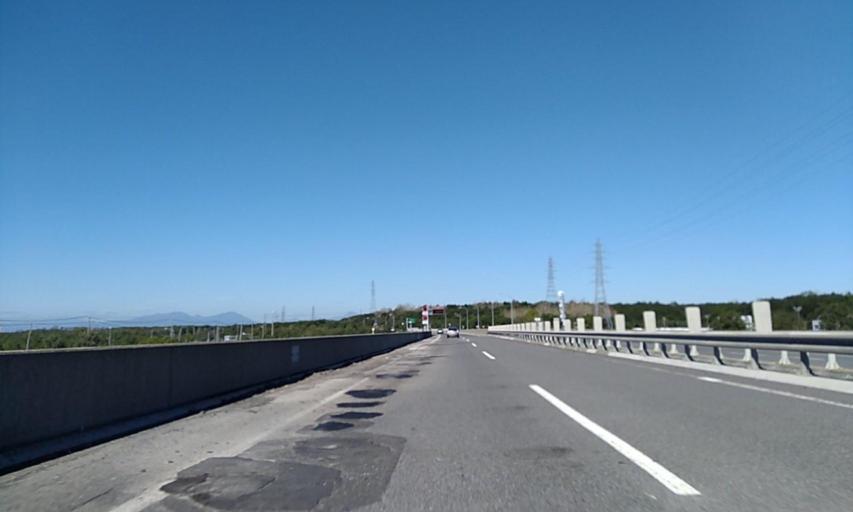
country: JP
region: Hokkaido
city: Tomakomai
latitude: 42.6712
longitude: 141.7900
